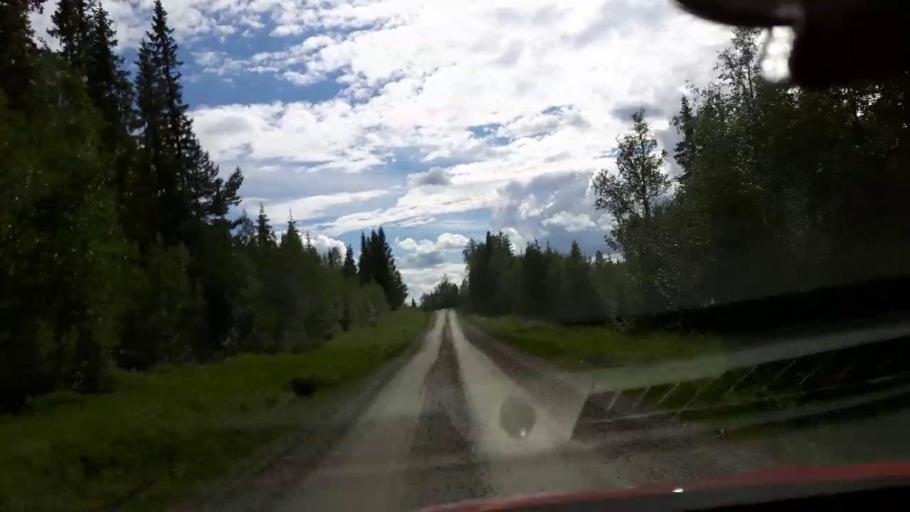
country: SE
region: Jaemtland
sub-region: Krokoms Kommun
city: Valla
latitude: 63.8982
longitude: 14.1792
